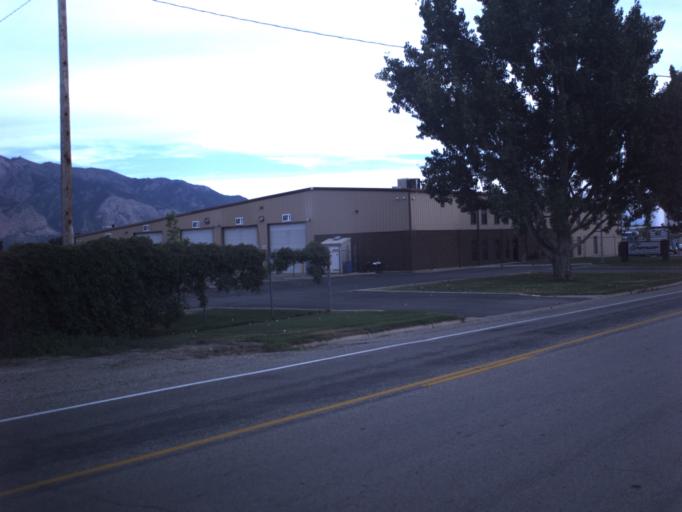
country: US
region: Utah
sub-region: Weber County
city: Farr West
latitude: 41.2748
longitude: -112.0282
